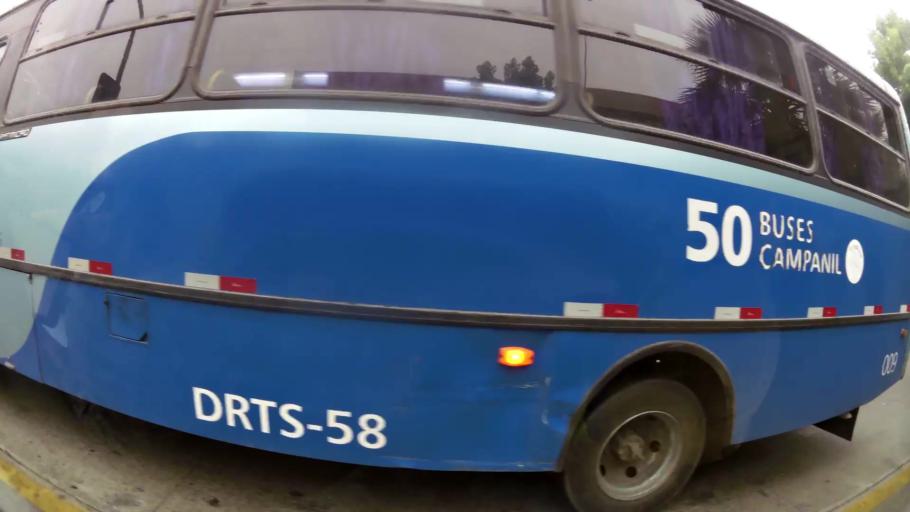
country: CL
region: Biobio
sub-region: Provincia de Concepcion
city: Concepcion
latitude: -36.8220
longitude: -73.0430
